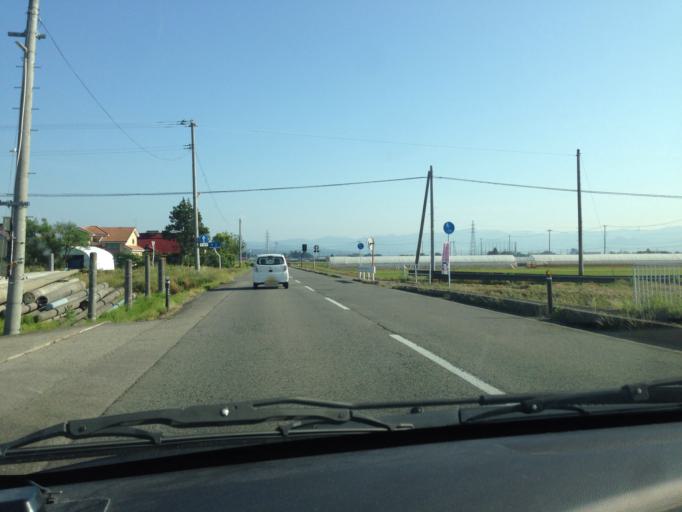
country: JP
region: Fukushima
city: Kitakata
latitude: 37.5448
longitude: 139.8314
